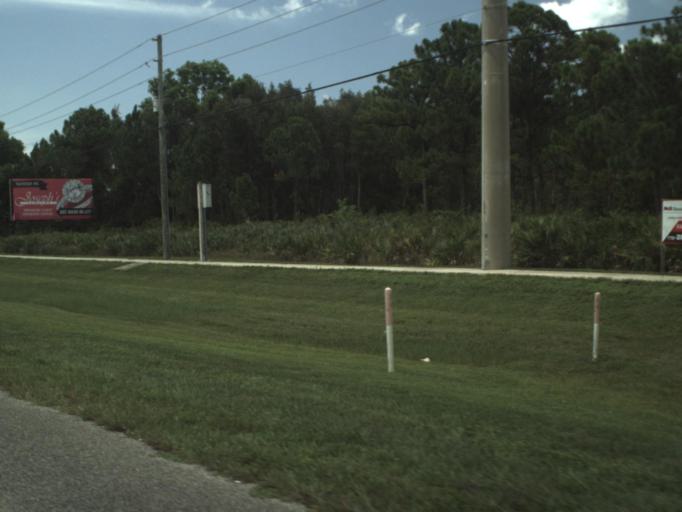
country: US
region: Florida
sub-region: Martin County
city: Port Salerno
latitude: 27.1378
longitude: -80.2093
